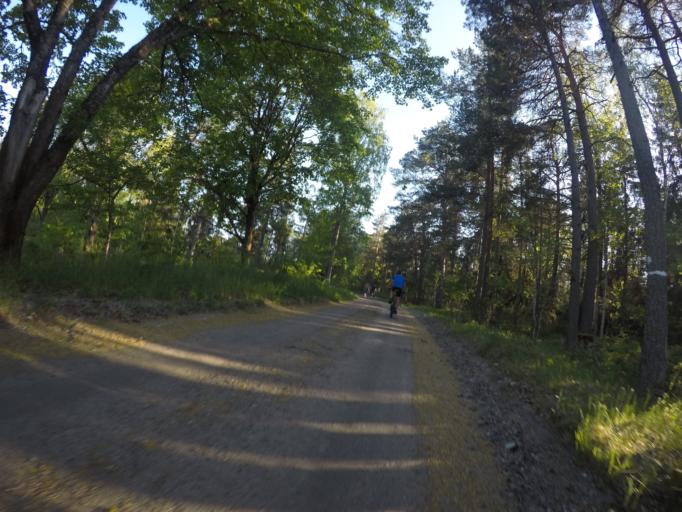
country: SE
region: Soedermanland
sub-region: Eskilstuna Kommun
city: Eskilstuna
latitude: 59.3479
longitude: 16.5333
